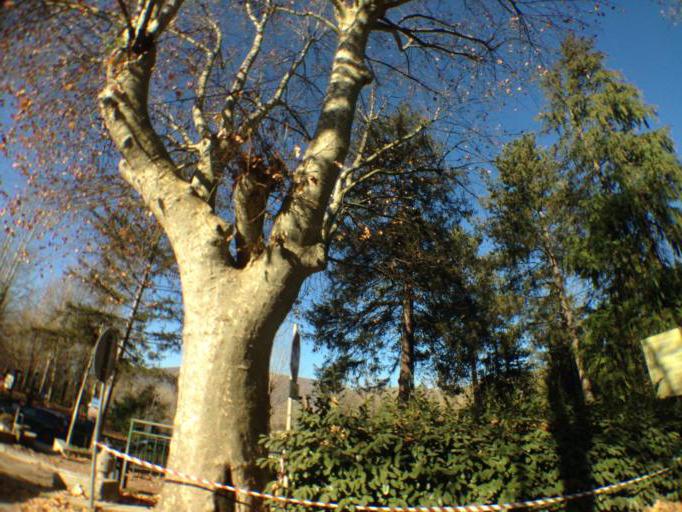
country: IT
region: Umbria
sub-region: Provincia di Perugia
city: Norcia
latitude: 42.7951
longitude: 13.0922
